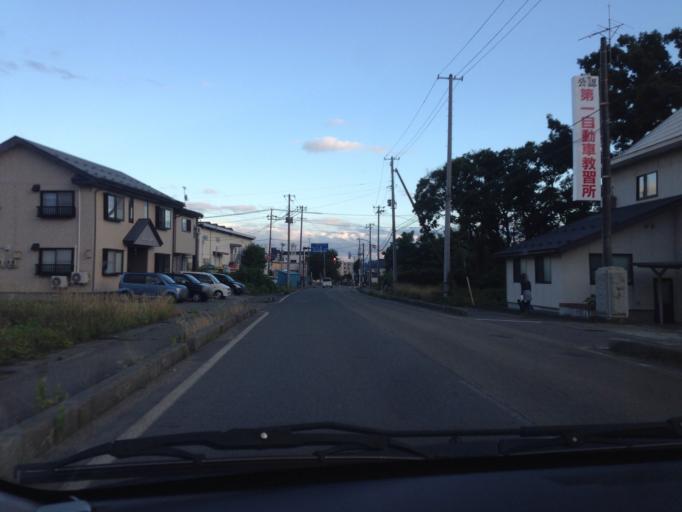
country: JP
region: Fukushima
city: Kitakata
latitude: 37.6661
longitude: 139.8656
